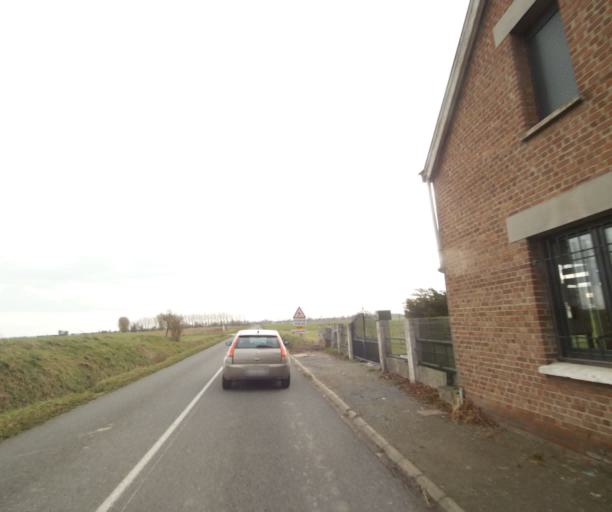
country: FR
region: Nord-Pas-de-Calais
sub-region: Departement du Nord
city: Quarouble
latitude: 50.3785
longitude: 3.6285
